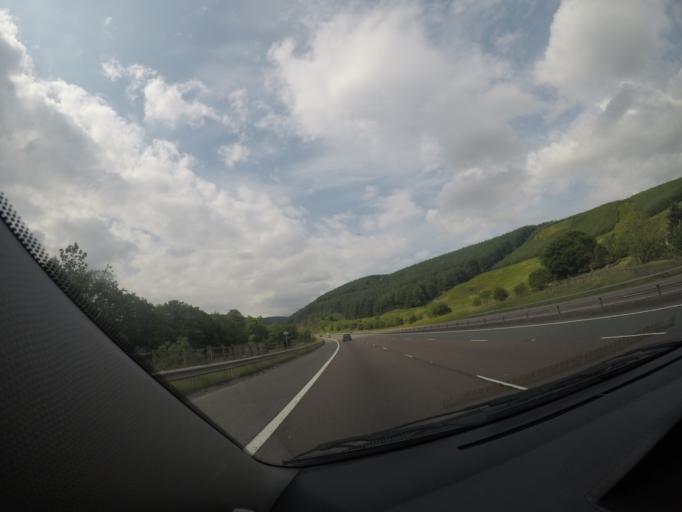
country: GB
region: Scotland
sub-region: Dumfries and Galloway
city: Moffat
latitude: 55.3896
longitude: -3.5228
